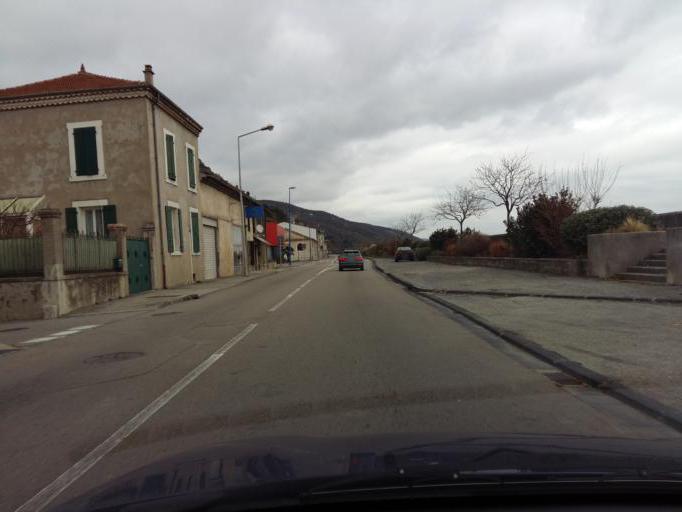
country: FR
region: Rhone-Alpes
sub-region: Departement de l'Ardeche
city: Le Pouzin
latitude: 44.7602
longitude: 4.7510
